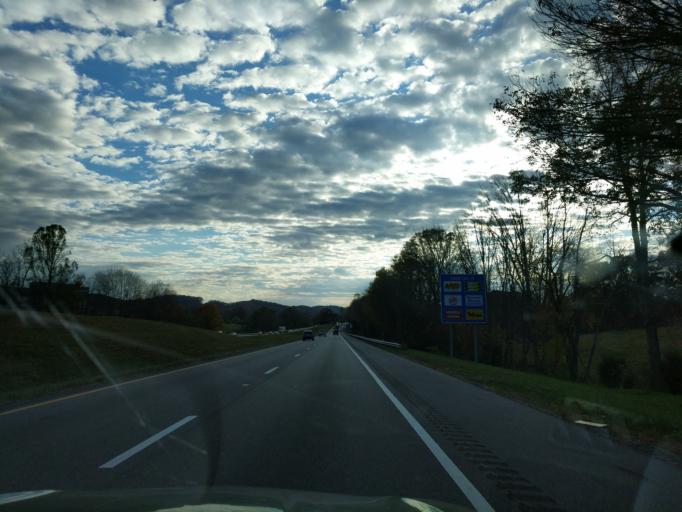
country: US
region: Virginia
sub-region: Washington County
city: Abingdon
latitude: 36.7262
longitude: -81.9113
